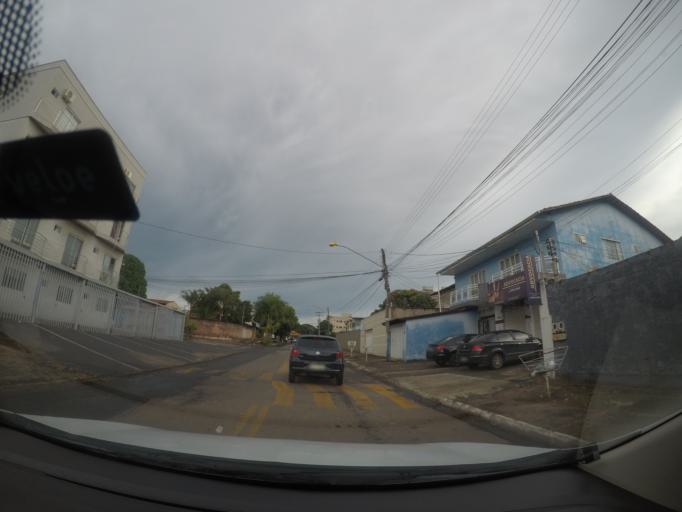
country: BR
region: Goias
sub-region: Goiania
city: Goiania
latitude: -16.6920
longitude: -49.3084
